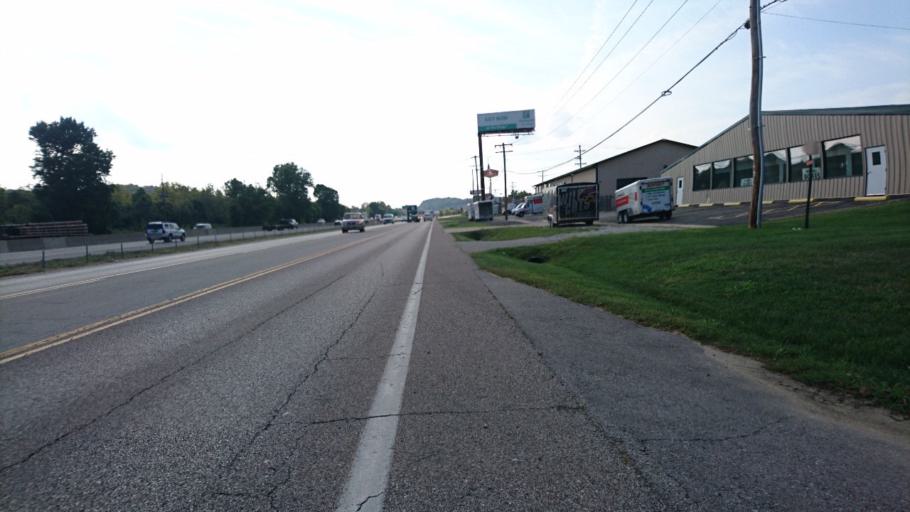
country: US
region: Missouri
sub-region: Saint Louis County
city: Eureka
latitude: 38.5046
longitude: -90.6602
